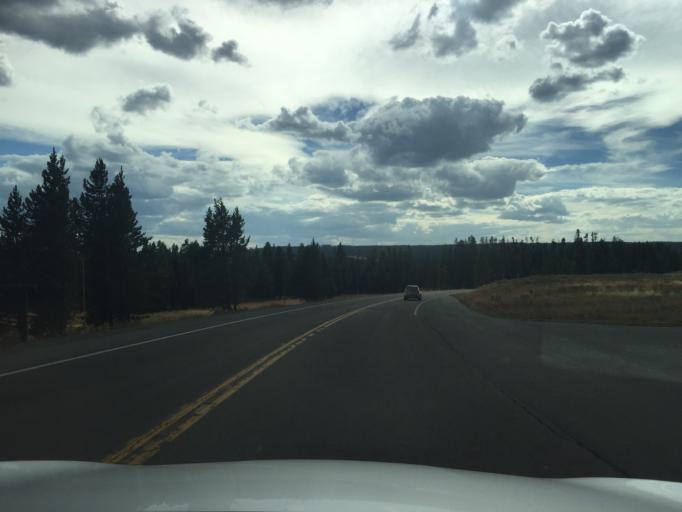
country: US
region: Montana
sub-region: Gallatin County
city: West Yellowstone
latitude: 44.7236
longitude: -110.4942
